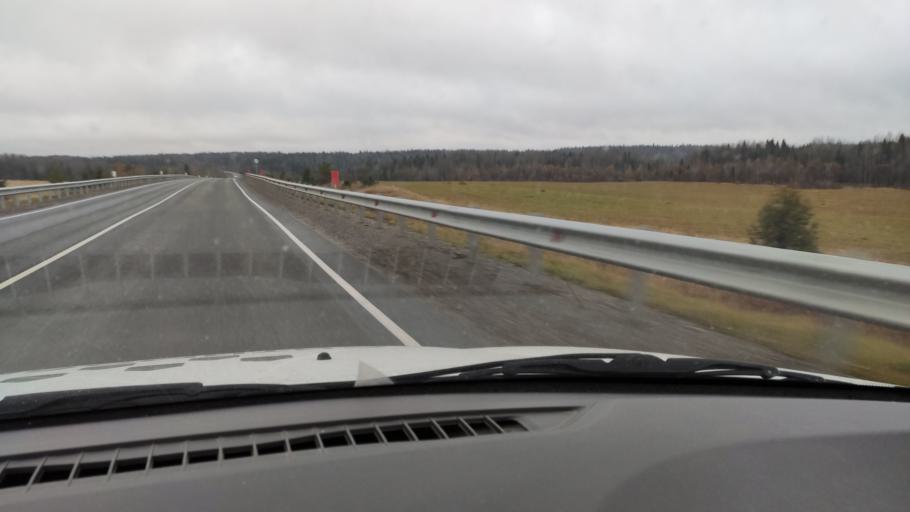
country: RU
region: Kirov
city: Omutninsk
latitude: 58.6869
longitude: 52.1373
